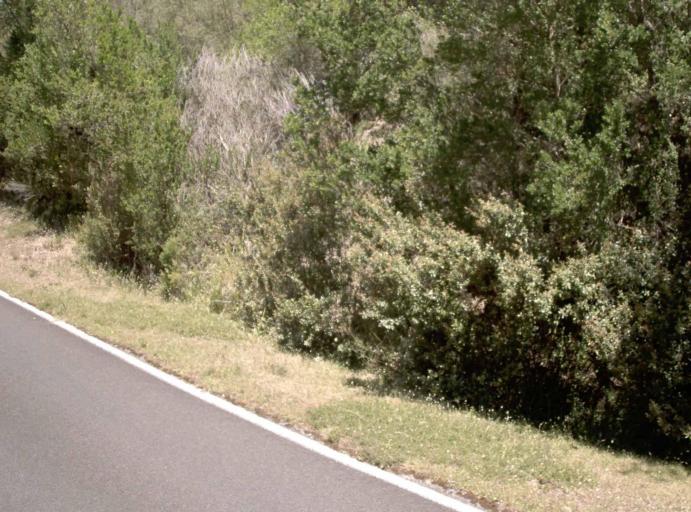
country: AU
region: Victoria
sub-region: Latrobe
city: Morwell
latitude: -38.8650
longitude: 146.2614
